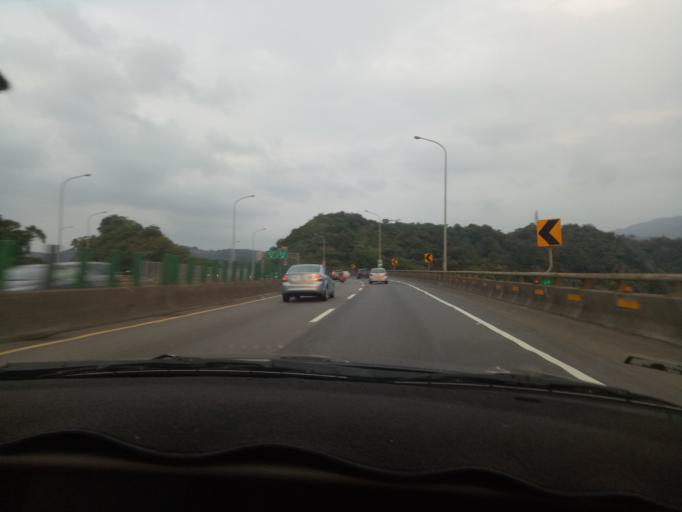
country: TW
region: Taiwan
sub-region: Keelung
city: Keelung
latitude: 25.1047
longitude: 121.7280
